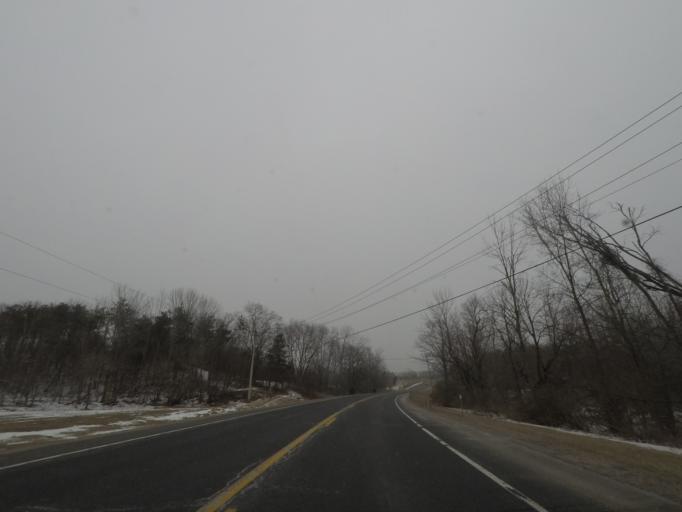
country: US
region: New York
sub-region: Albany County
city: Delmar
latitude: 42.5651
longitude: -73.8285
